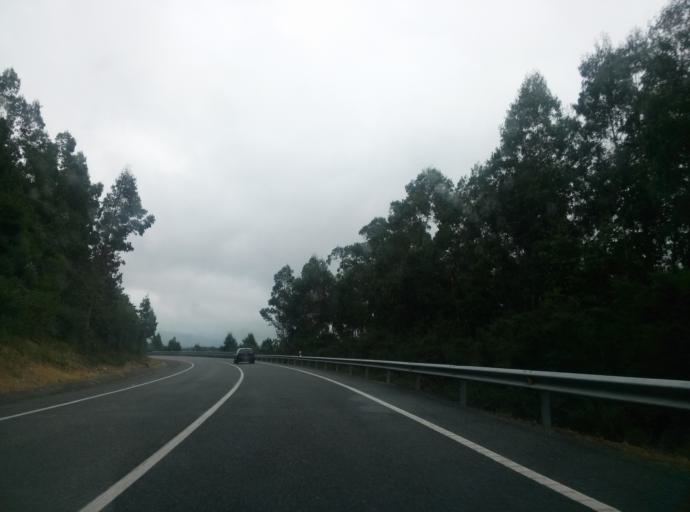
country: ES
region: Galicia
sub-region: Provincia de Lugo
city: Viveiro
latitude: 43.5595
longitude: -7.6448
